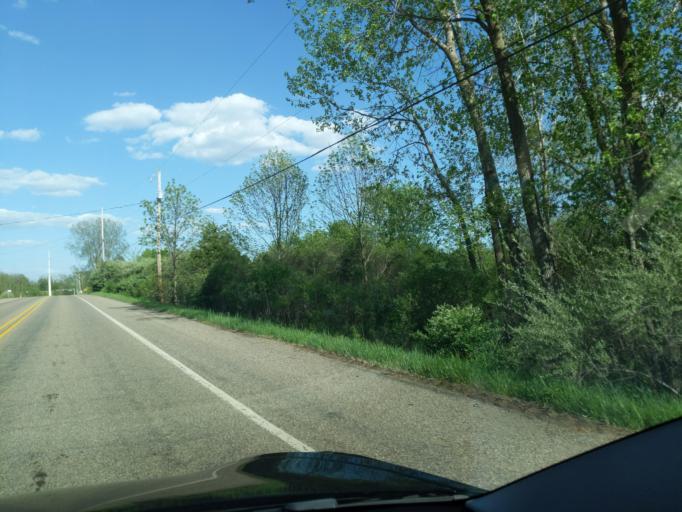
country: US
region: Michigan
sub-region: Eaton County
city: Dimondale
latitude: 42.6829
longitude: -84.6672
